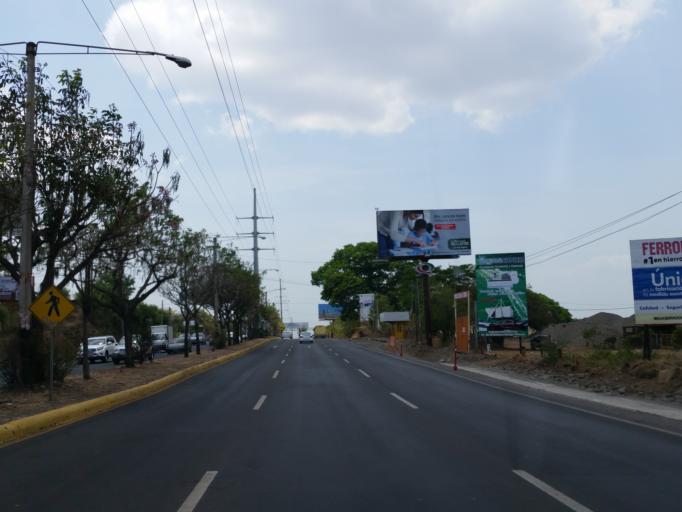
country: NI
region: Managua
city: Managua
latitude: 12.0930
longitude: -86.2367
